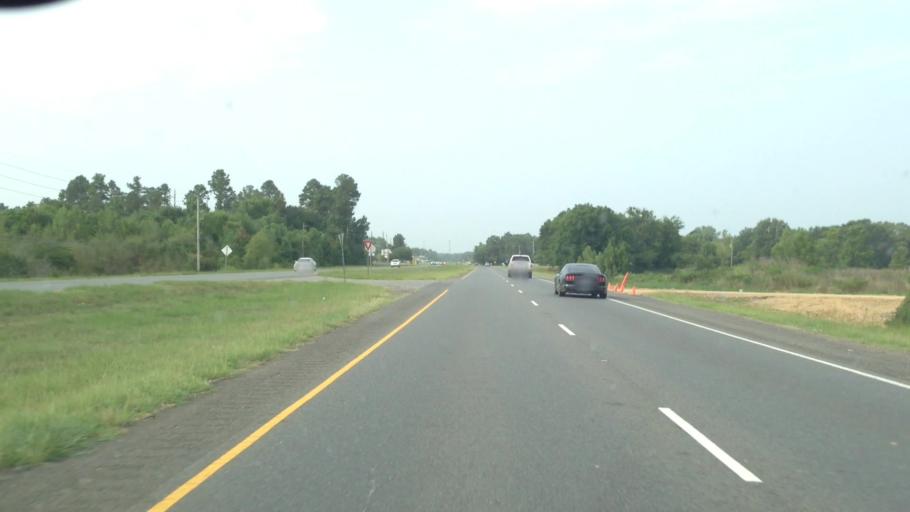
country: US
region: Louisiana
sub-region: De Soto Parish
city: Stonewall
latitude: 32.3752
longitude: -93.8220
